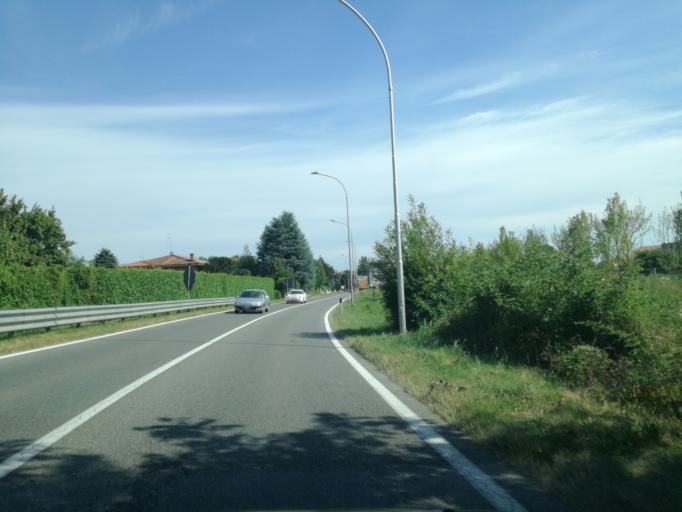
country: IT
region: Lombardy
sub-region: Provincia di Monza e Brianza
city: Bernareggio
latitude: 45.6491
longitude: 9.3984
